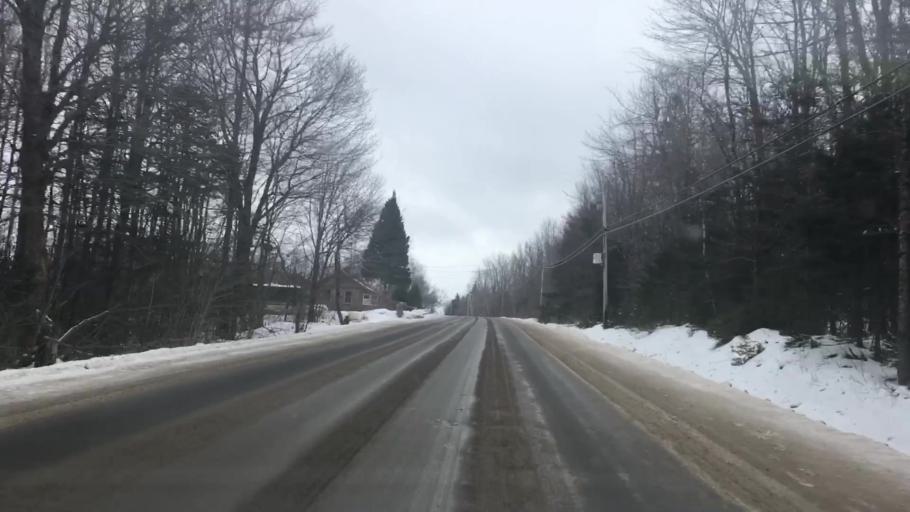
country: US
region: Maine
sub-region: Washington County
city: East Machias
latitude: 44.9880
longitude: -67.4590
